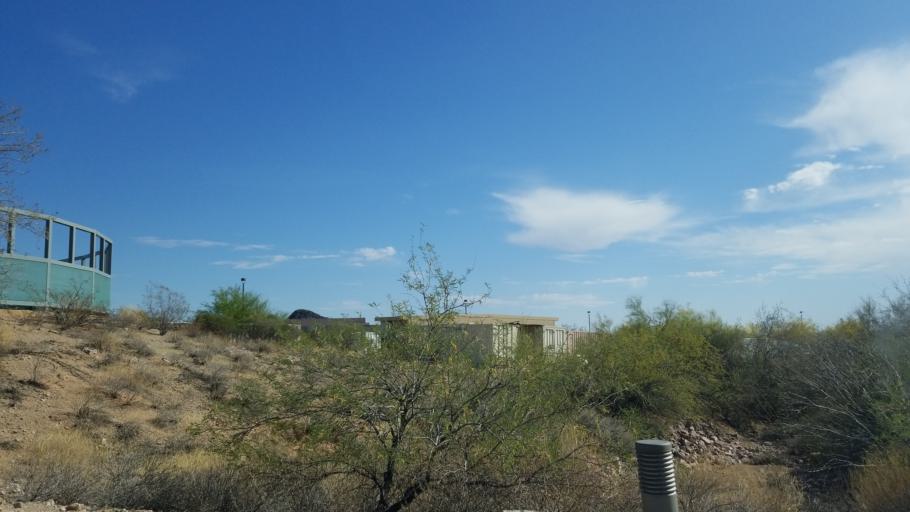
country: US
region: Arizona
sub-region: Maricopa County
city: Fountain Hills
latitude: 33.5876
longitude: -111.7955
